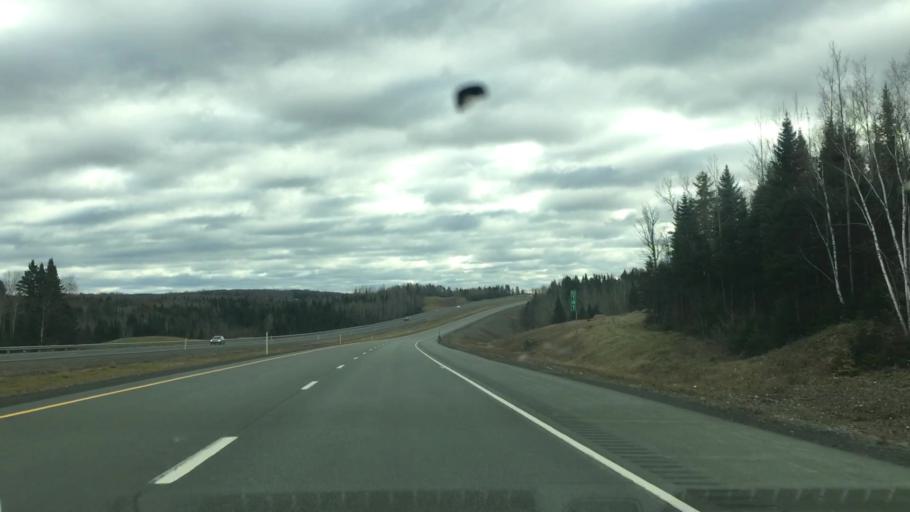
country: CA
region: New Brunswick
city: Florenceville-Bristol
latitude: 46.5423
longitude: -67.7161
